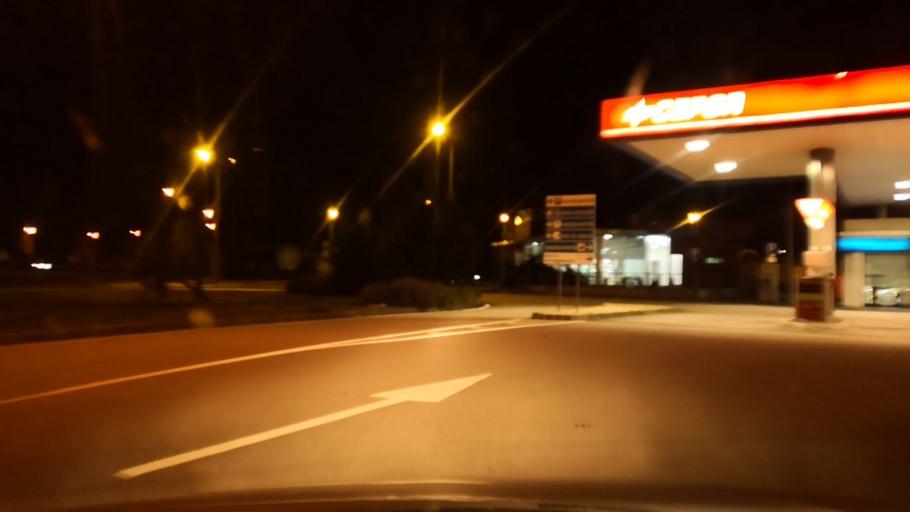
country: PT
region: Castelo Branco
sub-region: Concelho do Fundao
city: Fundao
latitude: 40.1904
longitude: -7.4865
